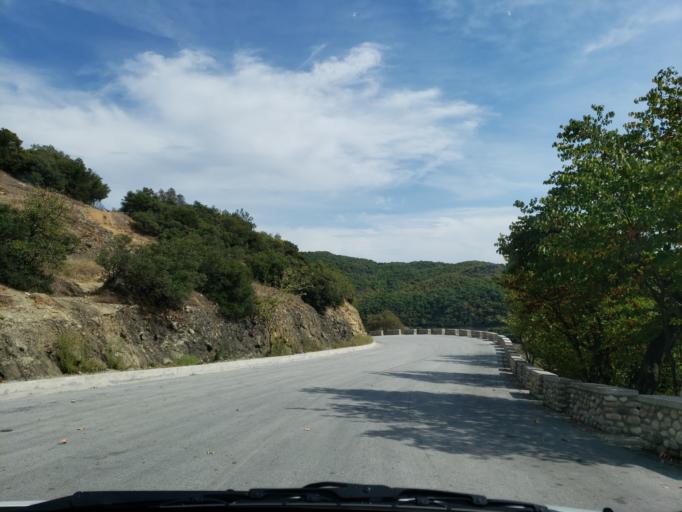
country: GR
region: Thessaly
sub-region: Trikala
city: Kastraki
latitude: 39.7266
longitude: 21.6286
